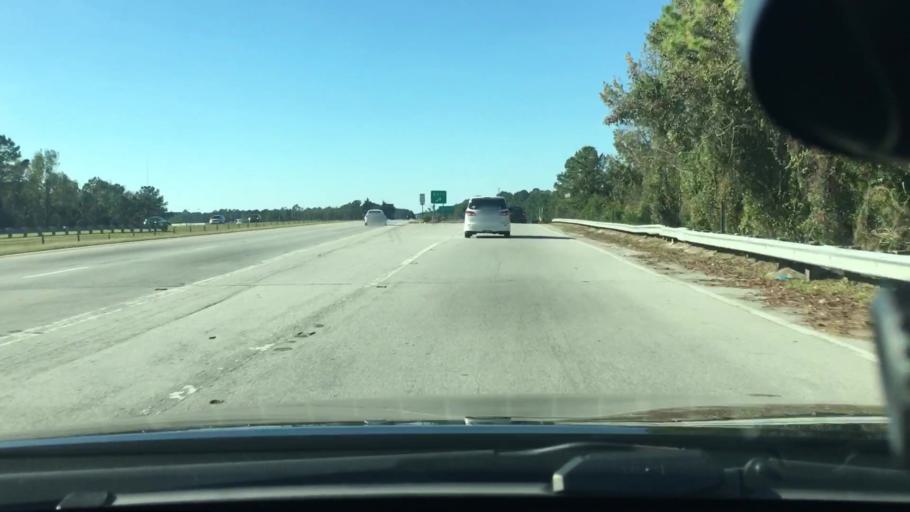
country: US
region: North Carolina
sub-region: Craven County
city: Trent Woods
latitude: 35.1019
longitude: -77.0809
